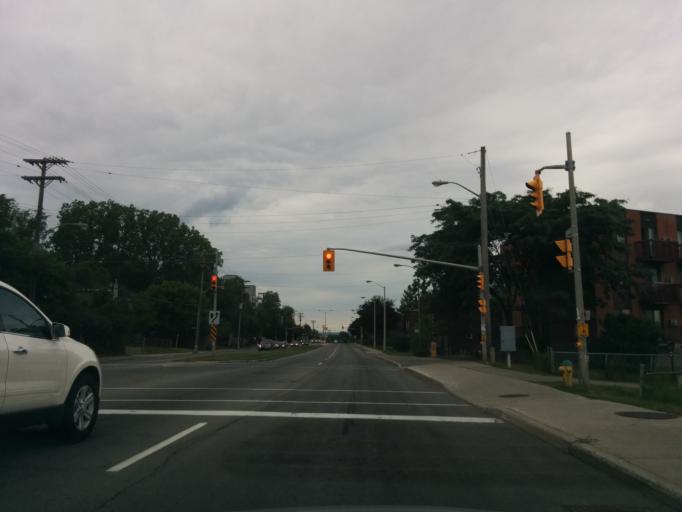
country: CA
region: Ontario
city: Ottawa
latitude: 45.3732
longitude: -75.7325
